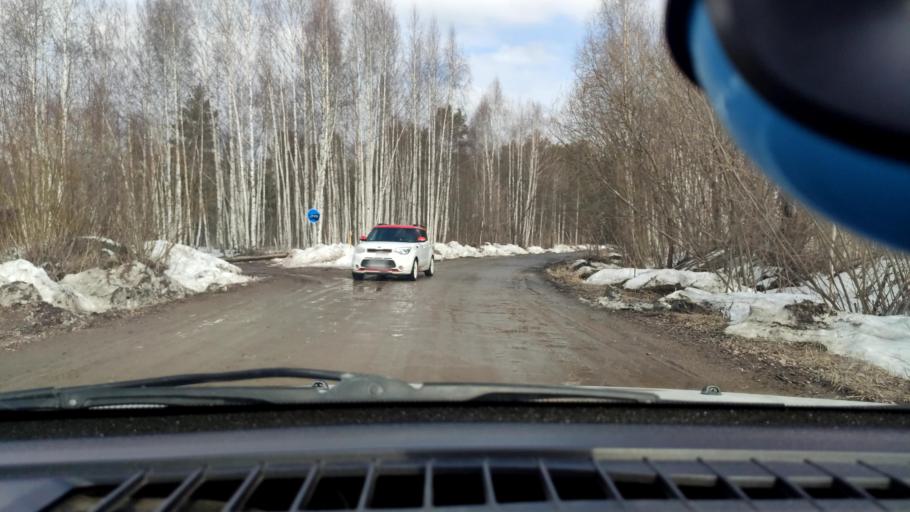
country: RU
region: Perm
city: Kondratovo
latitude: 58.0375
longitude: 56.0583
